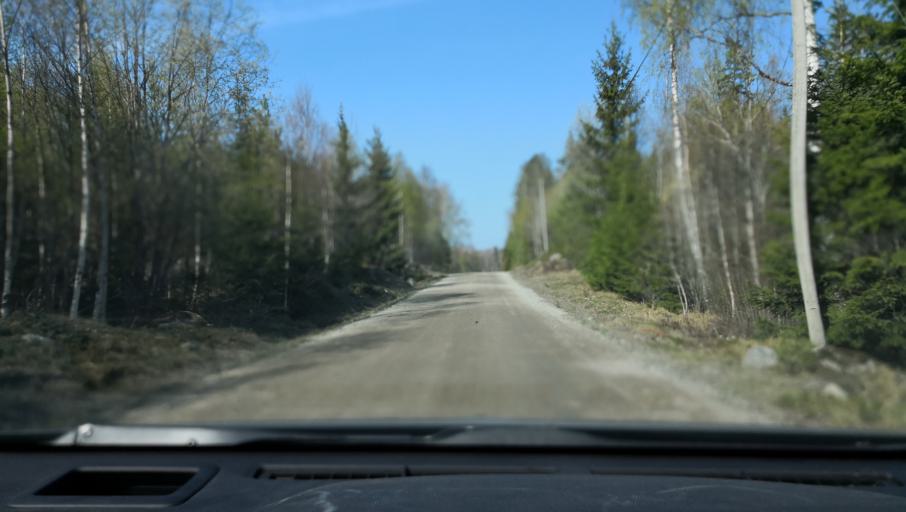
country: SE
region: Uppsala
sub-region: Heby Kommun
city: Heby
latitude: 60.0306
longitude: 16.7815
